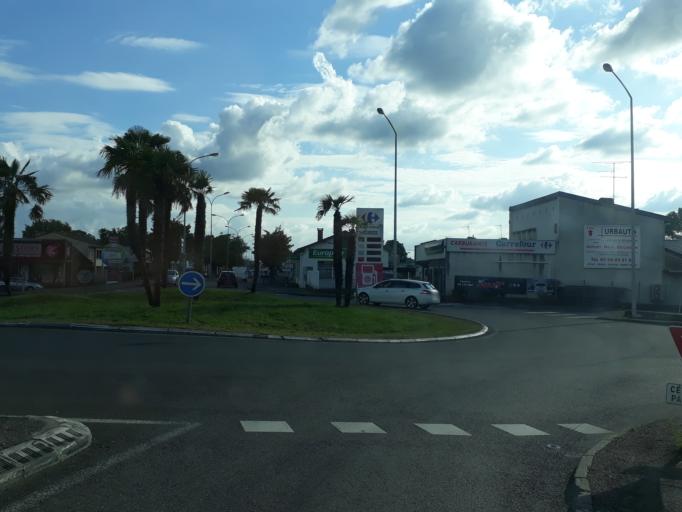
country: FR
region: Aquitaine
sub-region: Departement des Landes
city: Mont-de-Marsan
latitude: 43.9009
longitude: -0.4829
